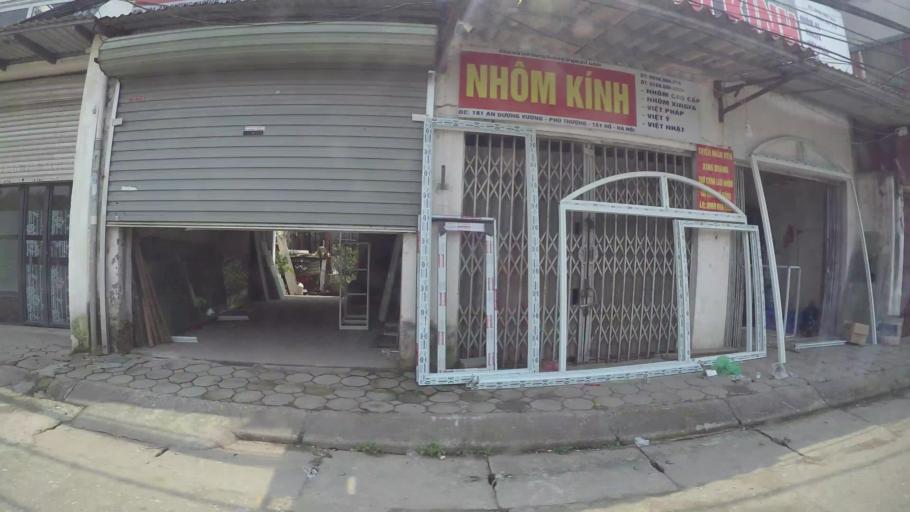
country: VN
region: Ha Noi
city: Tay Ho
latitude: 21.0897
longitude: 105.8060
